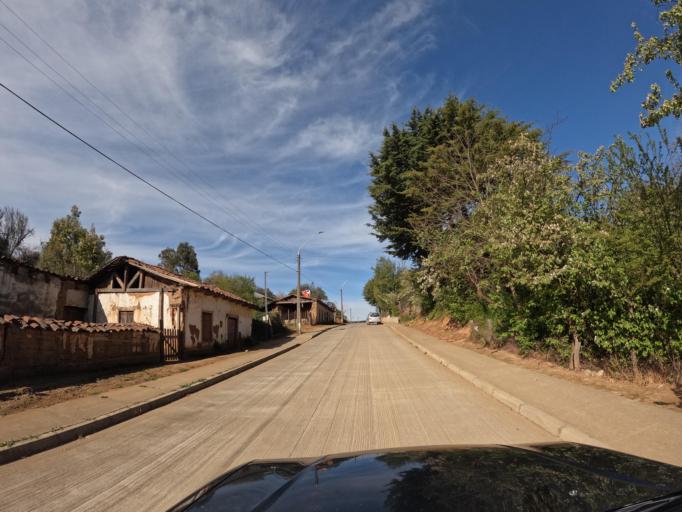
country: CL
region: Biobio
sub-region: Provincia de Biobio
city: La Laja
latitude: -37.1308
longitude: -72.7305
